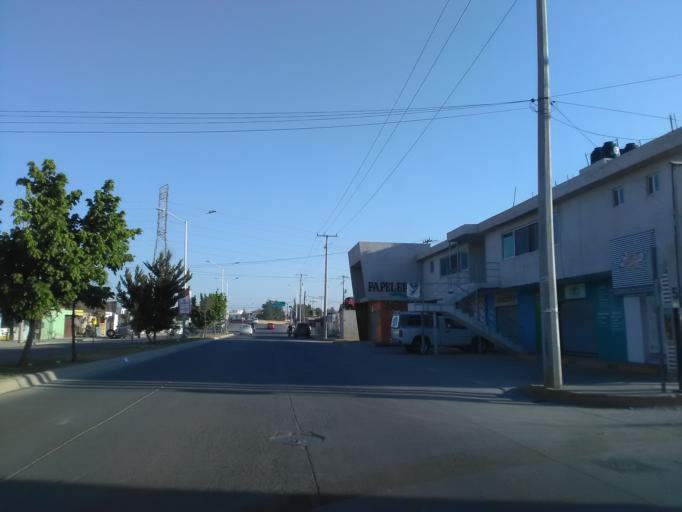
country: MX
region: Durango
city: Victoria de Durango
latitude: 24.0600
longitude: -104.6311
